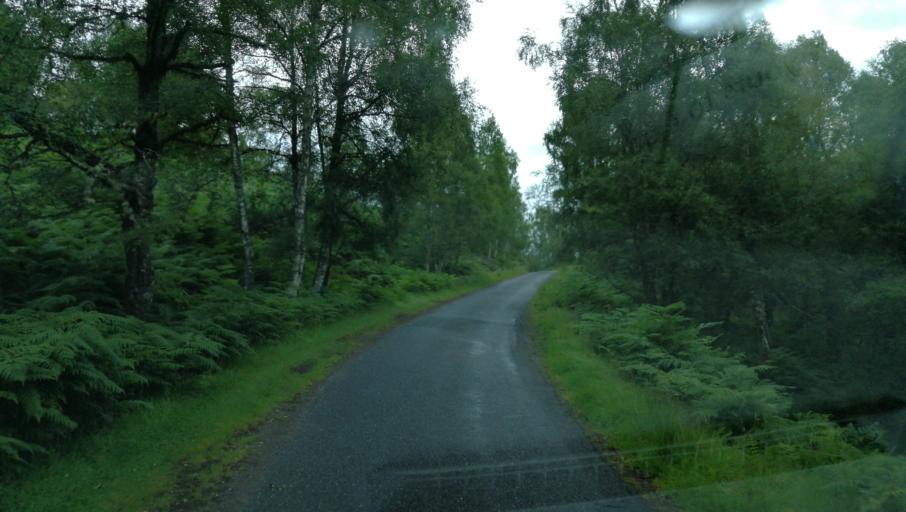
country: GB
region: Scotland
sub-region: Highland
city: Spean Bridge
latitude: 57.2872
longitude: -4.9209
